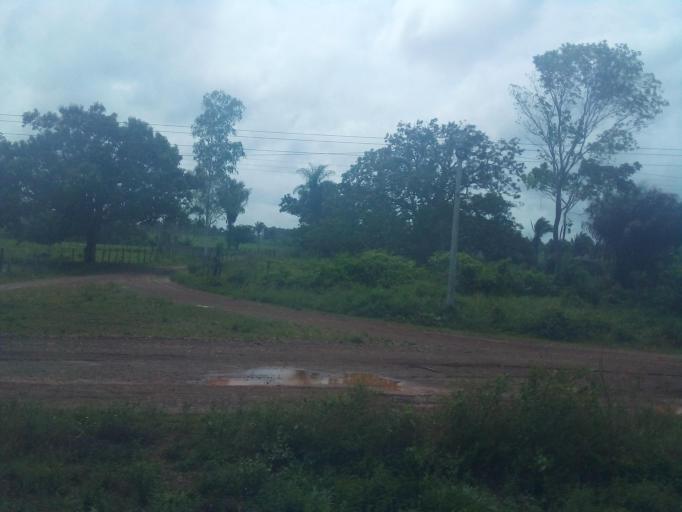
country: BR
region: Maranhao
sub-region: Arari
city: Arari
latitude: -3.4777
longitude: -44.6023
